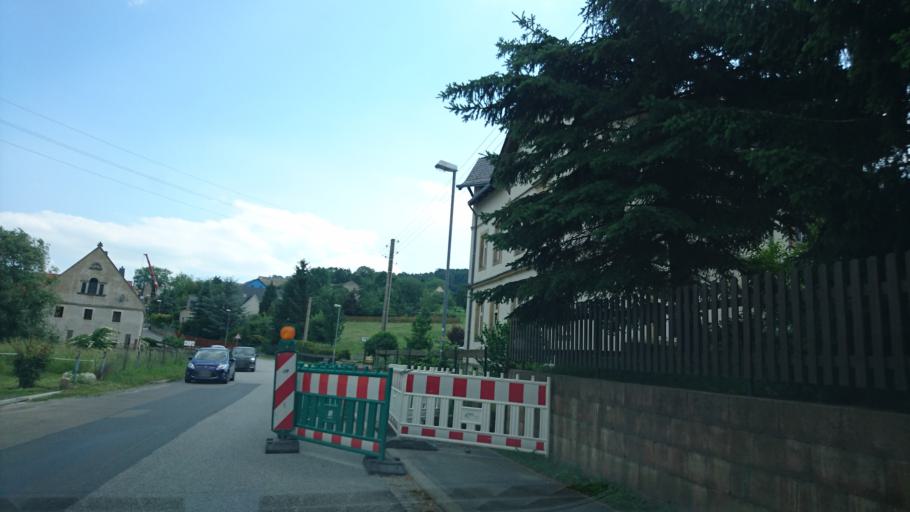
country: DE
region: Saxony
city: Dohma
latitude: 50.8999
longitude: 13.9572
